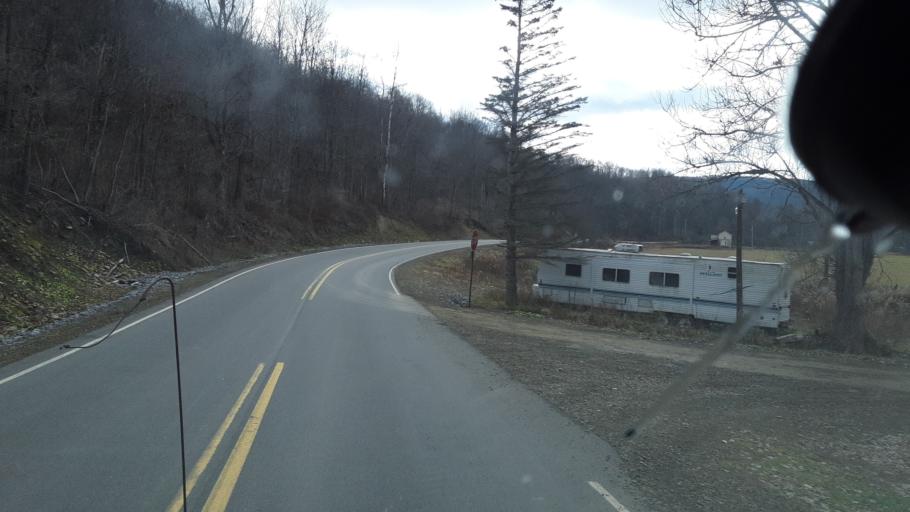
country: US
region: Pennsylvania
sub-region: Potter County
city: Galeton
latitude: 41.7987
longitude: -77.7125
